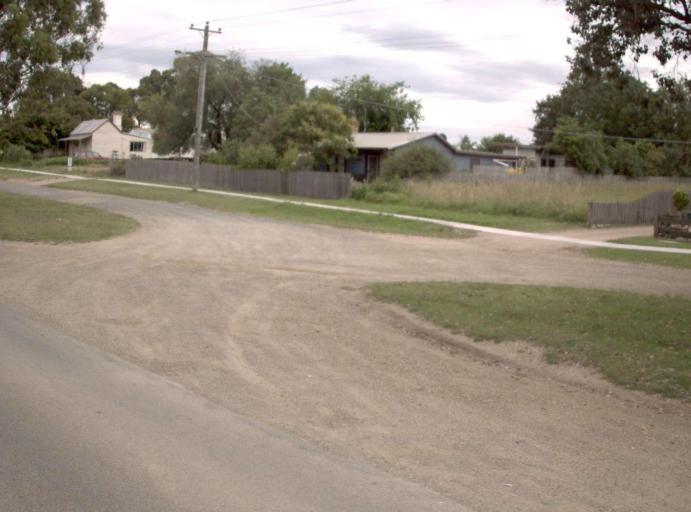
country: AU
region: Victoria
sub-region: East Gippsland
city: Bairnsdale
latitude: -37.8057
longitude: 147.6173
